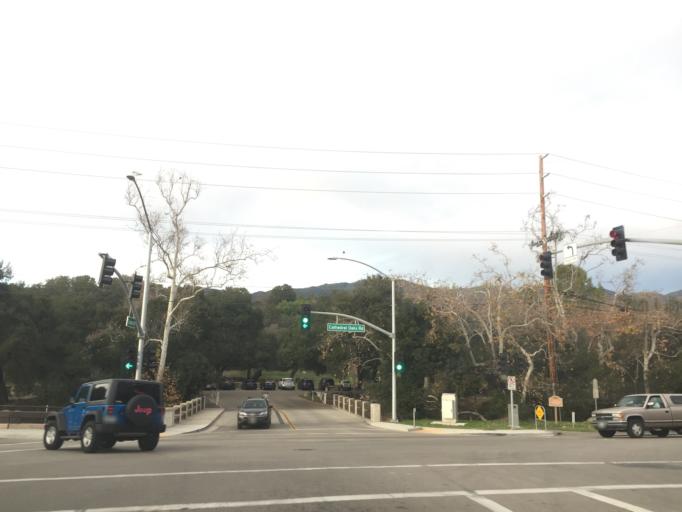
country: US
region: California
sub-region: Santa Barbara County
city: Goleta
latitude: 34.4511
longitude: -119.7901
